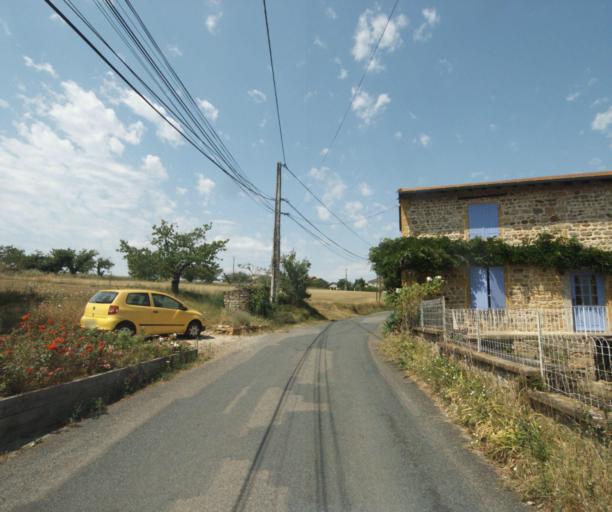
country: FR
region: Rhone-Alpes
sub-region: Departement du Rhone
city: Saint-Germain-Nuelles
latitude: 45.8456
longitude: 4.6299
